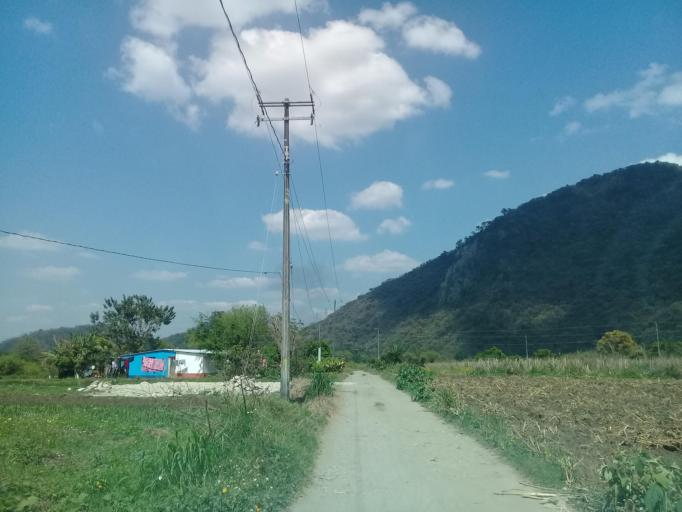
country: MX
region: Veracruz
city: Jalapilla
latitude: 18.8280
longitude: -97.0746
